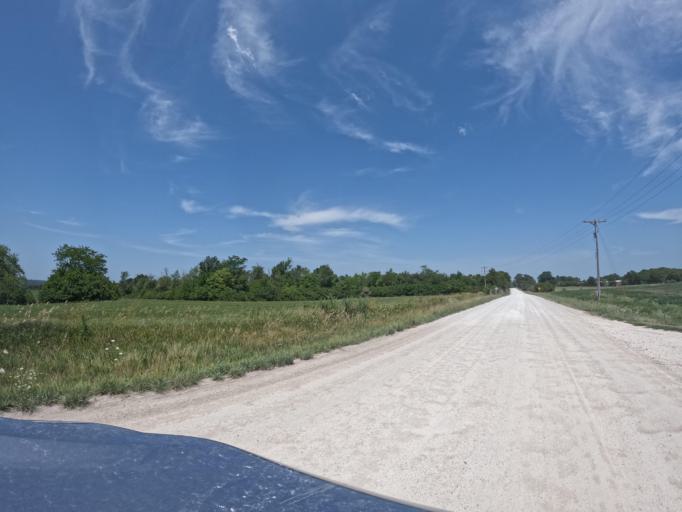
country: US
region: Iowa
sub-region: Henry County
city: Mount Pleasant
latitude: 40.9058
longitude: -91.5469
